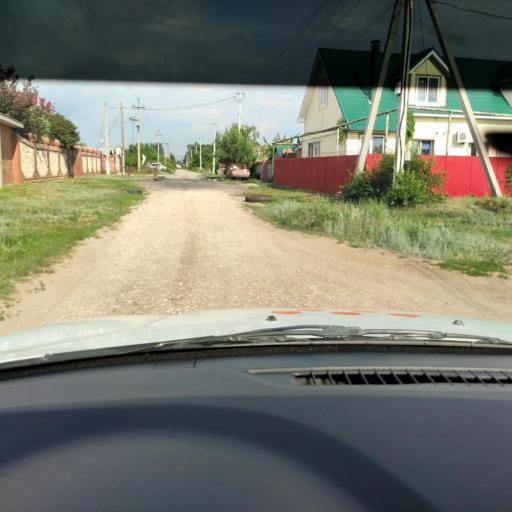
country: RU
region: Samara
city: Podstepki
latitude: 53.6142
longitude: 49.0348
